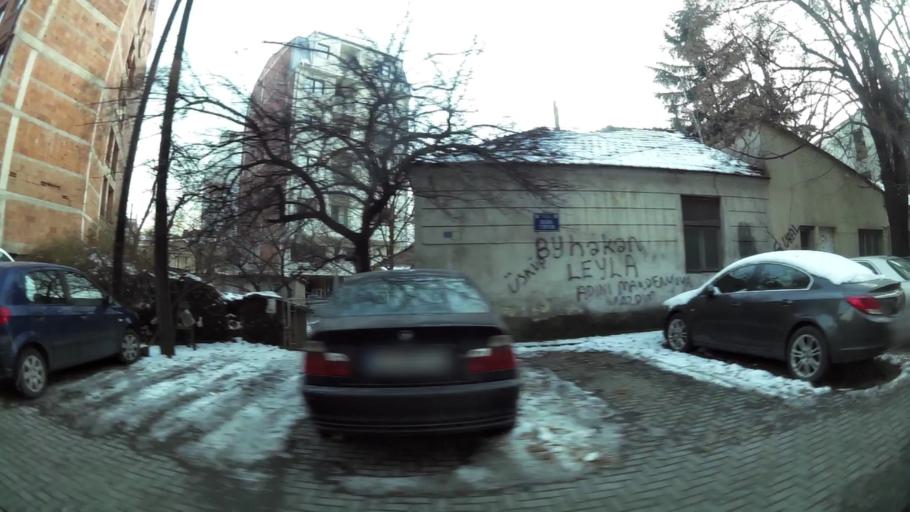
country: MK
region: Karpos
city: Skopje
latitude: 41.9920
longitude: 21.4216
